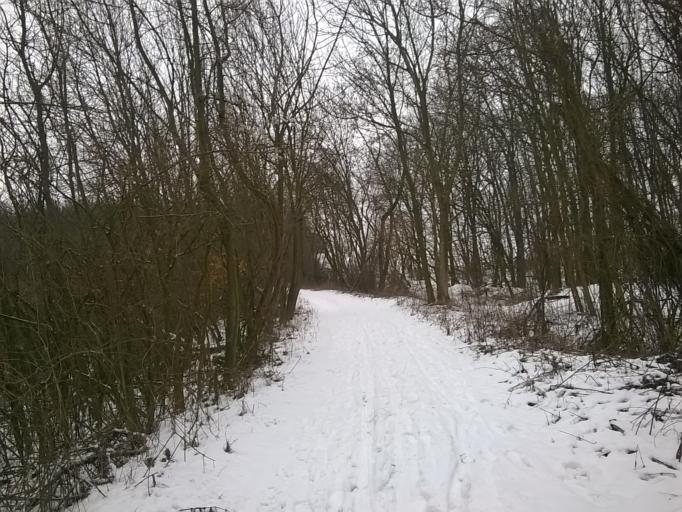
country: SK
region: Nitriansky
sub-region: Okres Nitra
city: Nitra
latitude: 48.2724
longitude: 18.0102
